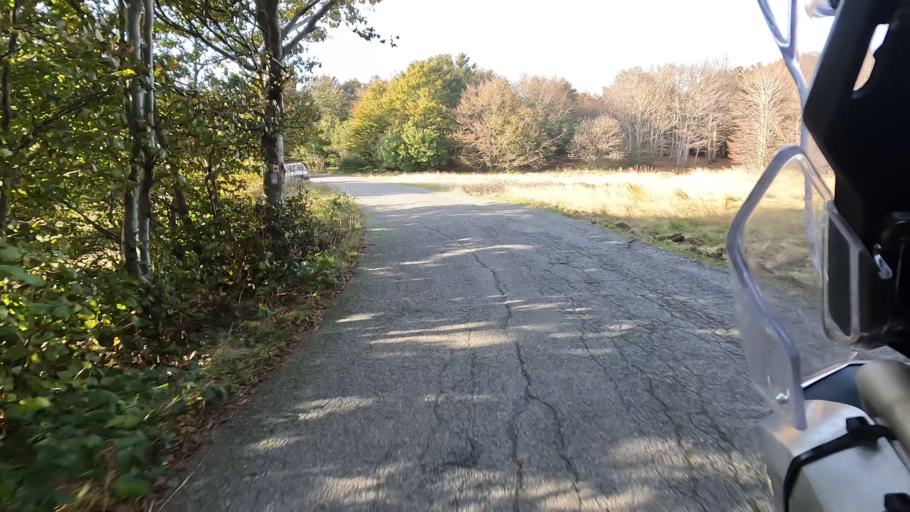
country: IT
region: Liguria
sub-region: Provincia di Genova
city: Sciarborasca
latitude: 44.4298
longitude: 8.5839
